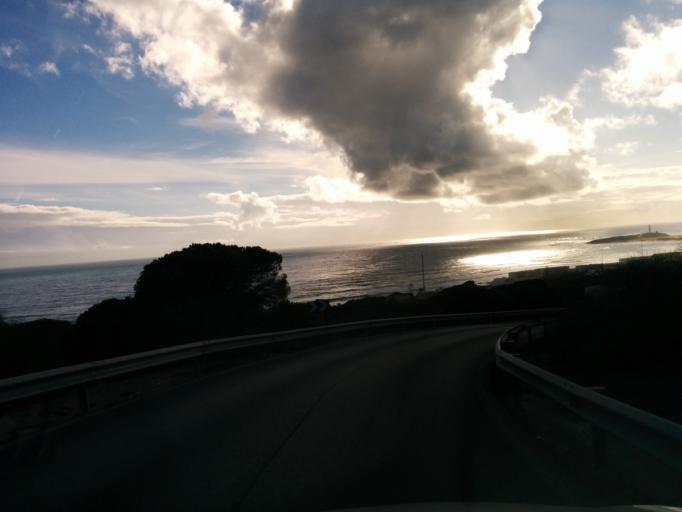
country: ES
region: Andalusia
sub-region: Provincia de Cadiz
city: Vejer de la Frontera
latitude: 36.1884
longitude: -6.0047
